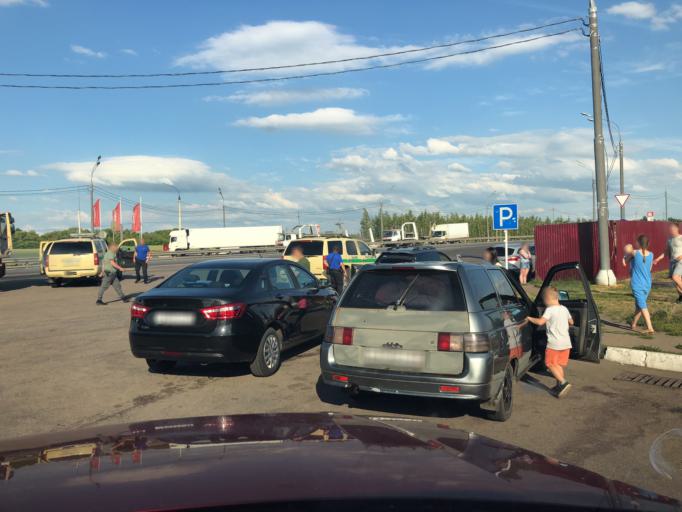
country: RU
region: Lipetsk
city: Zadonsk
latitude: 52.4262
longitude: 38.8288
